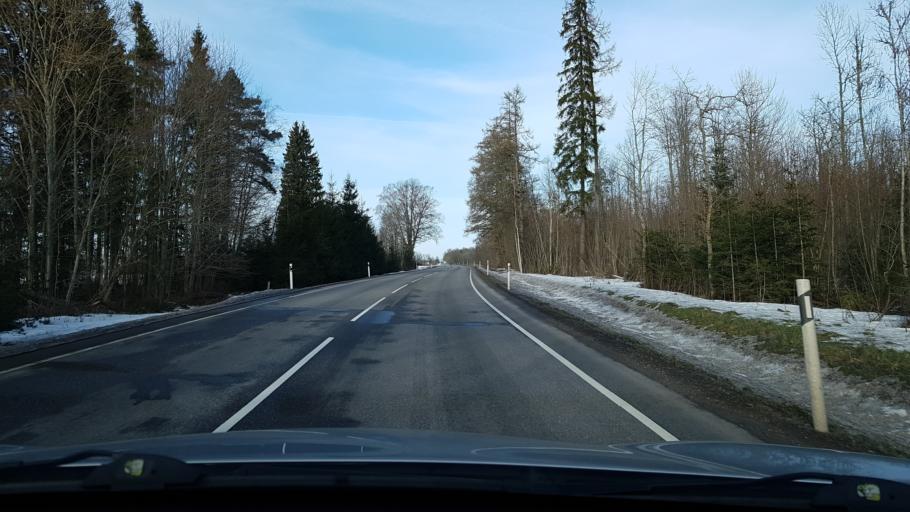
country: EE
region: Viljandimaa
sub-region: Abja vald
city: Abja-Paluoja
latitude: 58.3075
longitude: 25.2994
